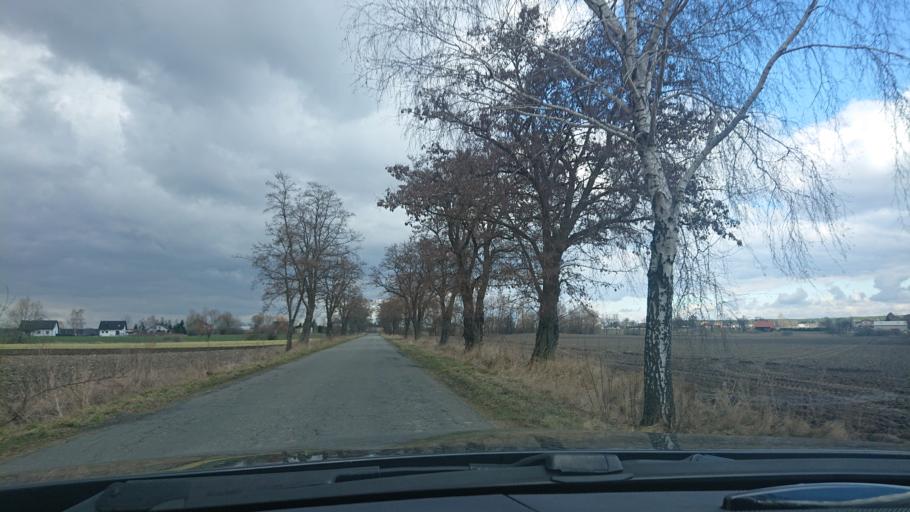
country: PL
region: Greater Poland Voivodeship
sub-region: Powiat gnieznienski
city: Trzemeszno
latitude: 52.5785
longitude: 17.7101
